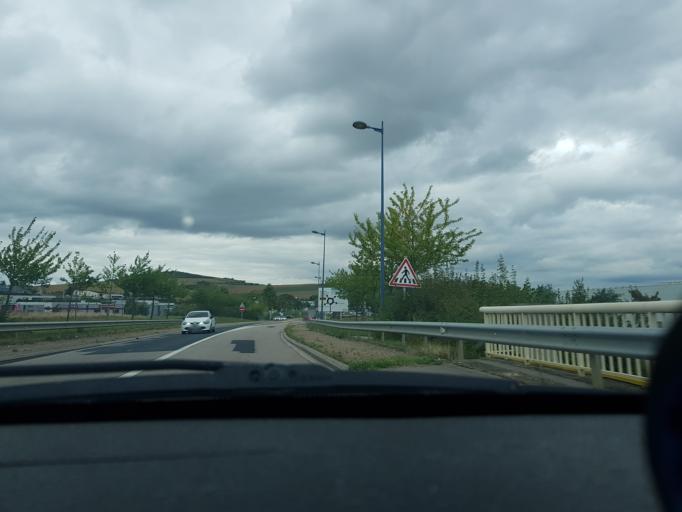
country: FR
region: Lorraine
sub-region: Departement de Meurthe-et-Moselle
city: Pulnoy
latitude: 48.7057
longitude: 6.2425
